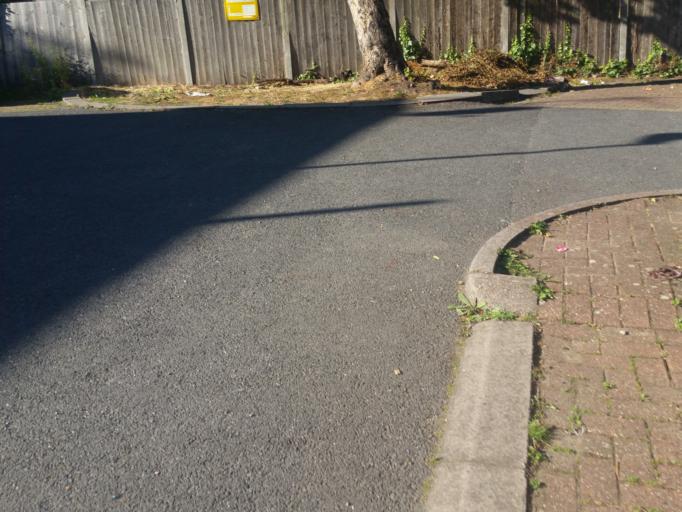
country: GB
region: England
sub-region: Greater London
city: Crouch End
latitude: 51.5844
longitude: -0.1163
